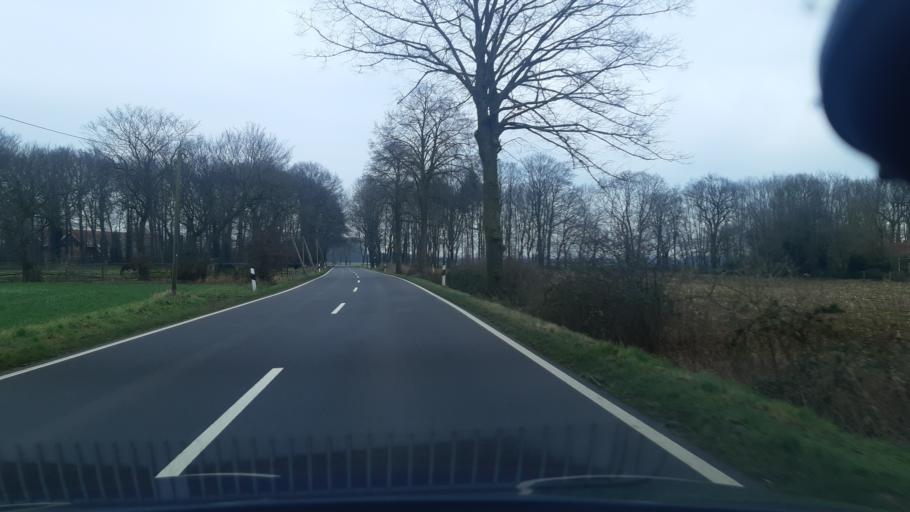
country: DE
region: Lower Saxony
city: Cloppenburg
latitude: 52.8165
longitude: 7.9935
